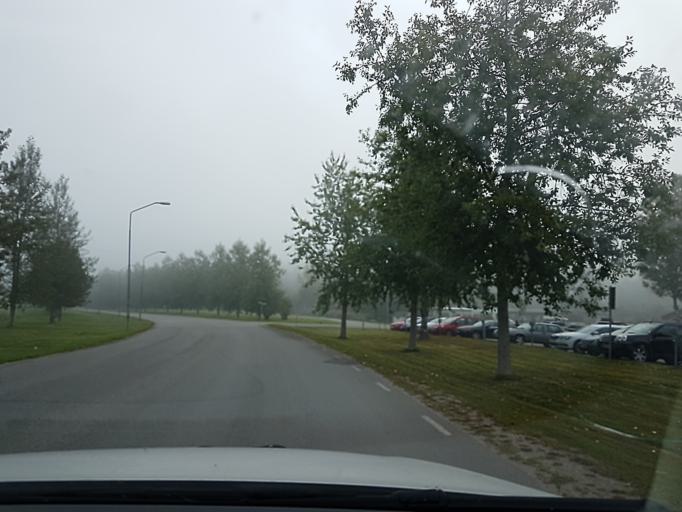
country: SE
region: Norrbotten
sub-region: Pitea Kommun
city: Pitea
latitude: 65.3158
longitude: 21.5014
